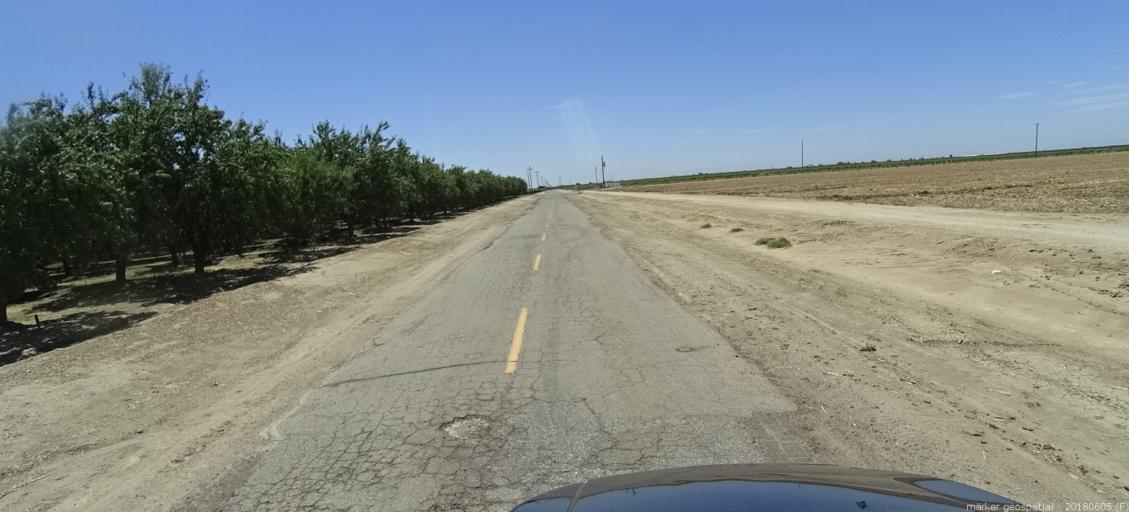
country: US
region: California
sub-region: Madera County
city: Chowchilla
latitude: 37.0999
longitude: -120.3651
